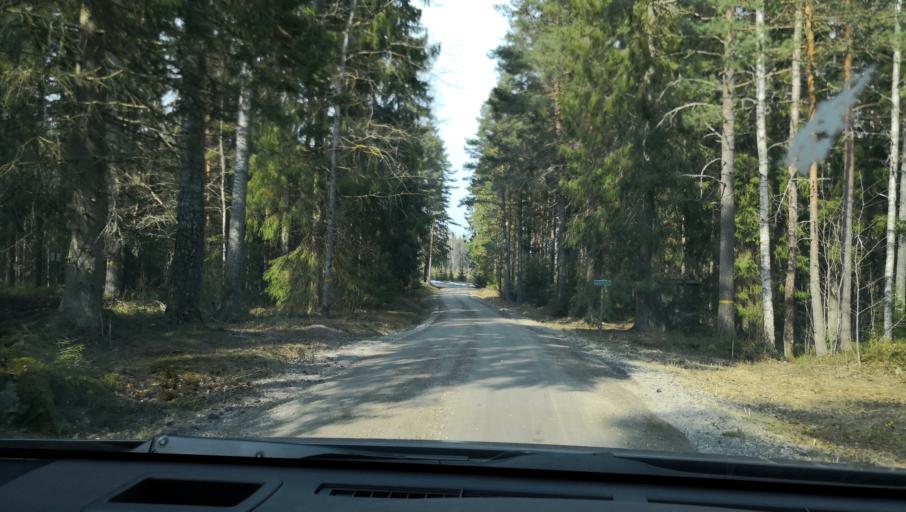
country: SE
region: OErebro
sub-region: Lindesbergs Kommun
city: Frovi
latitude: 59.3588
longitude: 15.4342
